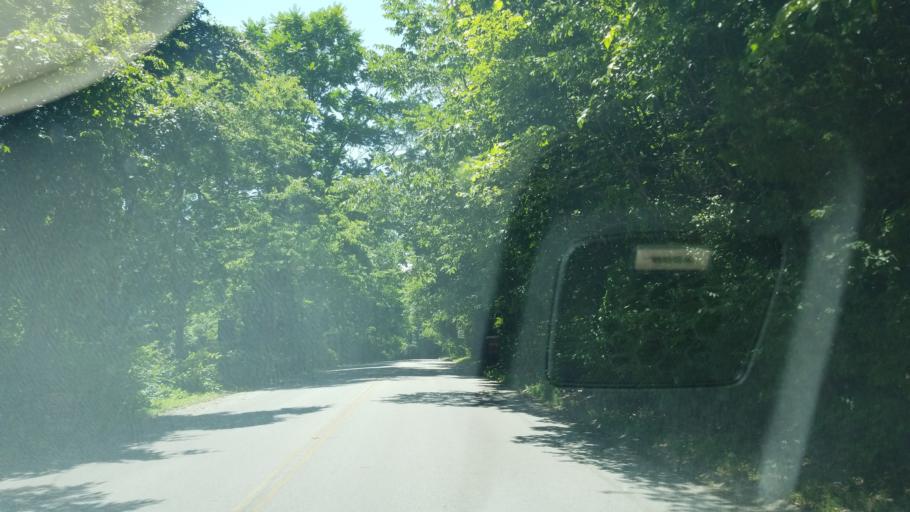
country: US
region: Tennessee
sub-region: Davidson County
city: Forest Hills
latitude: 36.0568
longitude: -86.8240
